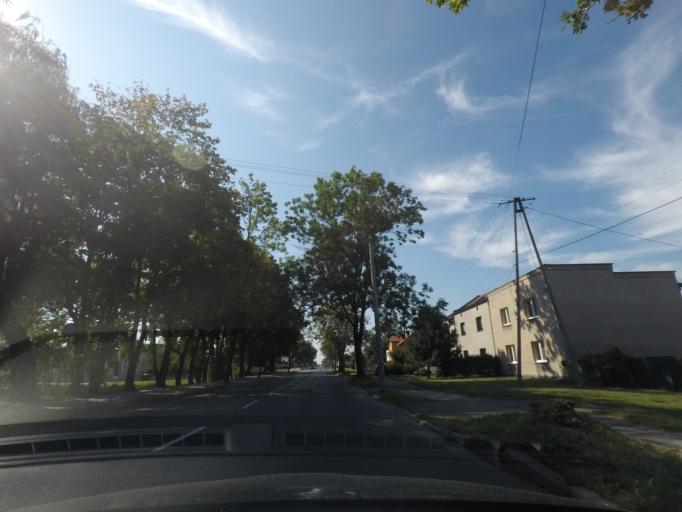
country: PL
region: Silesian Voivodeship
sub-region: Zory
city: Zory
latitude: 50.0503
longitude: 18.6885
